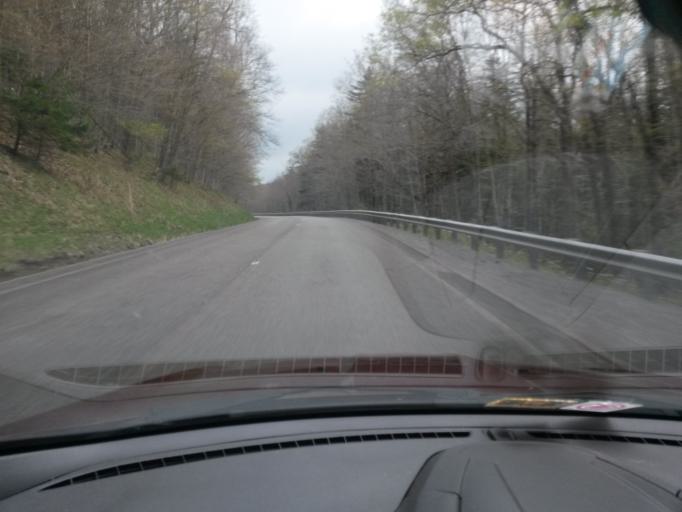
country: US
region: West Virginia
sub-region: Randolph County
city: Elkins
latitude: 38.6276
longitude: -79.9012
